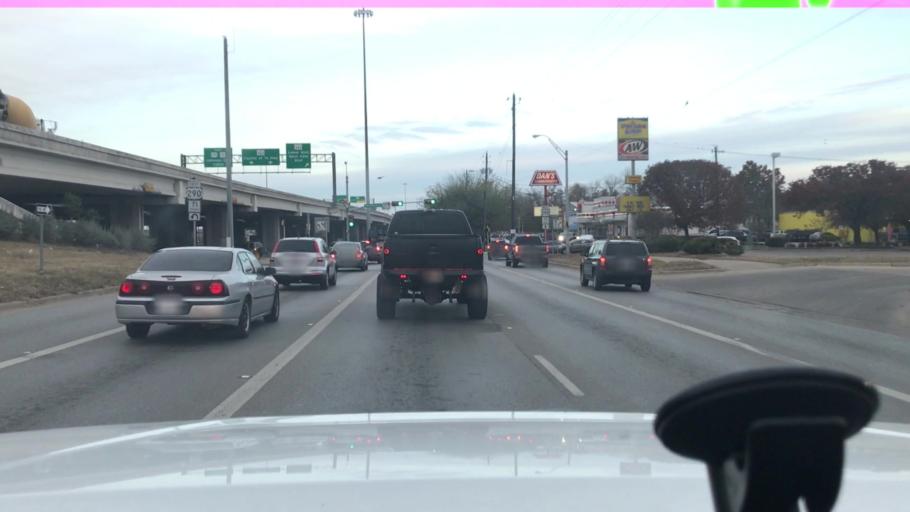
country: US
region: Texas
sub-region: Travis County
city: Rollingwood
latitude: 30.2299
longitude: -97.7873
